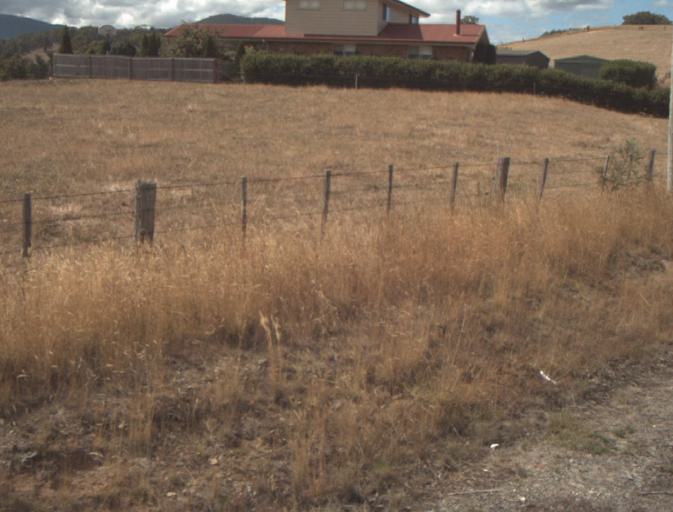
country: AU
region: Tasmania
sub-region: Launceston
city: Mayfield
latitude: -41.2380
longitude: 147.1484
